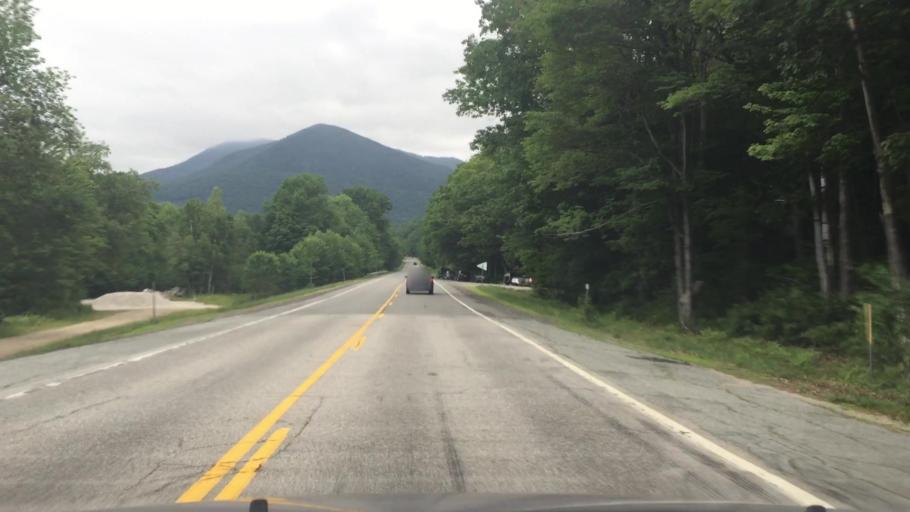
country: US
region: New Hampshire
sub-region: Carroll County
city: North Conway
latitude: 44.1047
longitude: -71.3524
